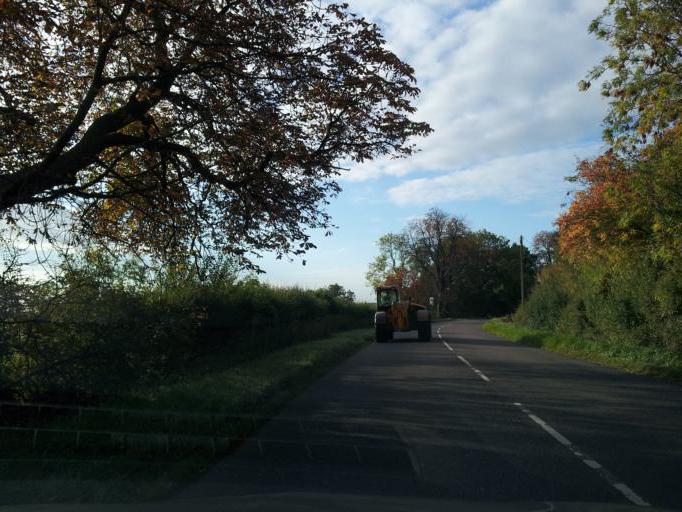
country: GB
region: England
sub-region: Lincolnshire
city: Long Bennington
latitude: 52.9811
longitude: -0.8065
